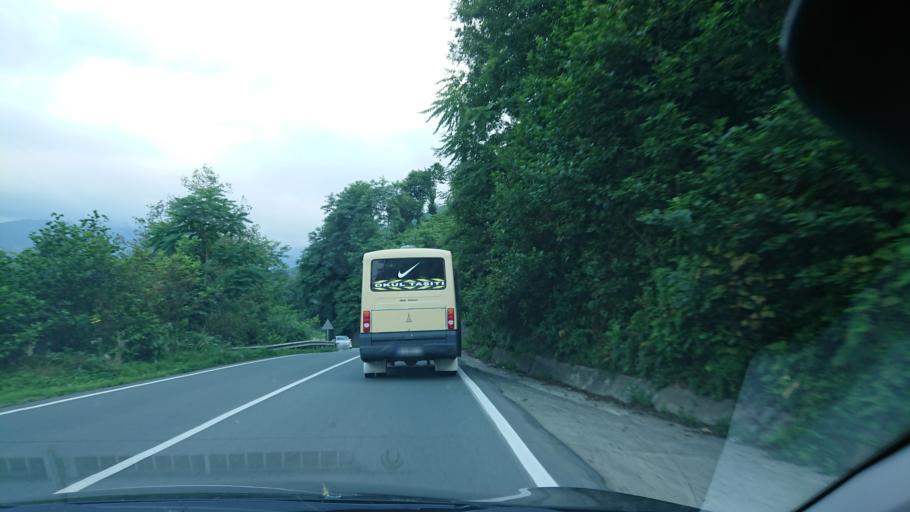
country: TR
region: Rize
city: Cayeli
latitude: 41.0729
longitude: 40.7111
